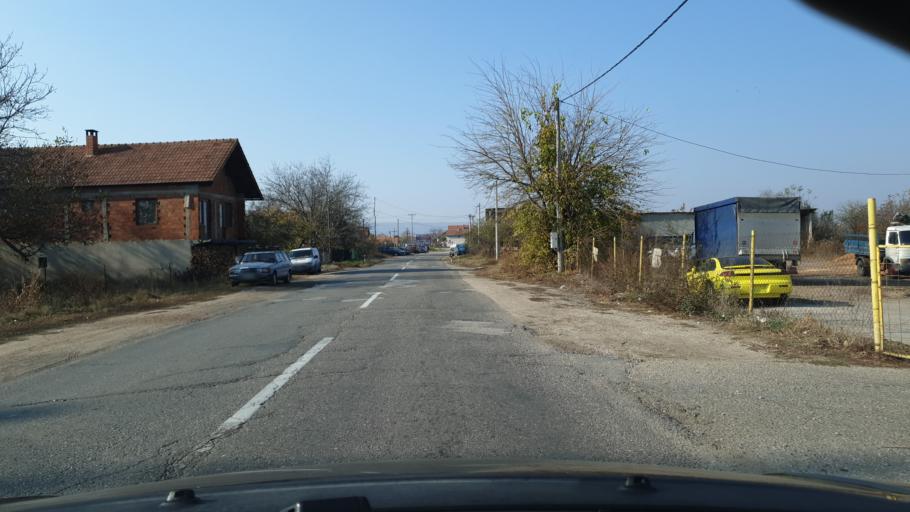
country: RS
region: Central Serbia
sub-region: Borski Okrug
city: Negotin
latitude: 44.2242
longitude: 22.5494
